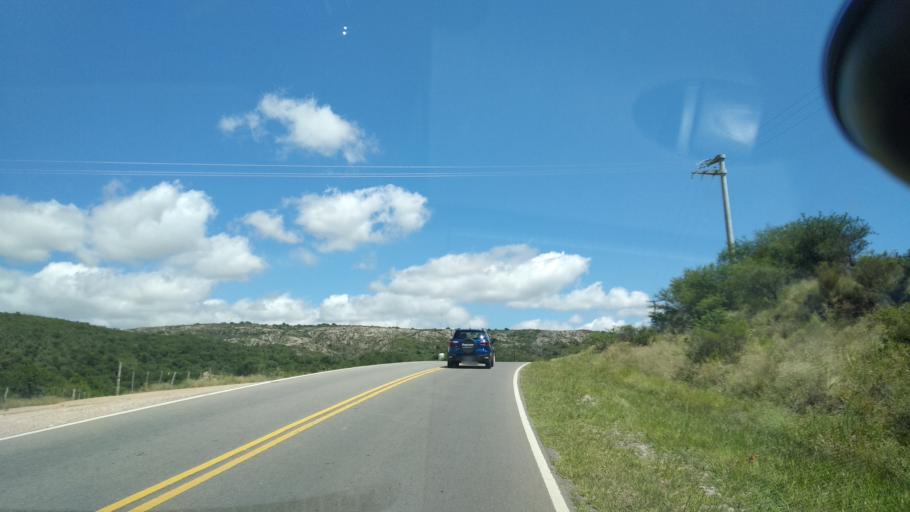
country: AR
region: Cordoba
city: Villa Cura Brochero
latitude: -31.6952
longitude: -65.0424
